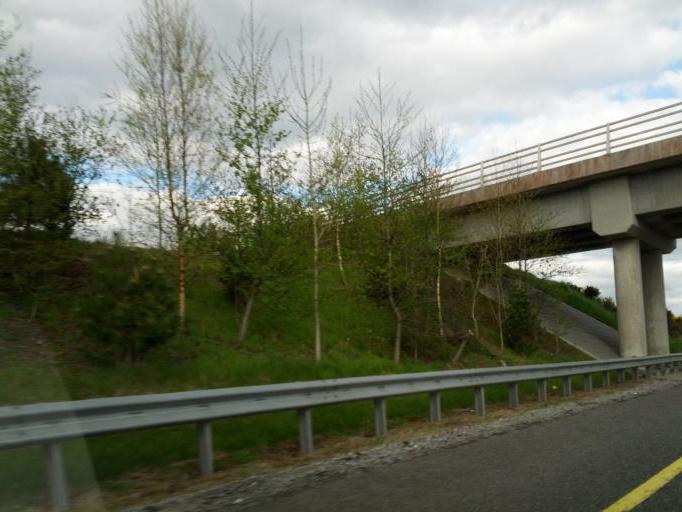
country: IE
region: Leinster
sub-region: An Iarmhi
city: Moate
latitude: 53.3870
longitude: -7.7375
